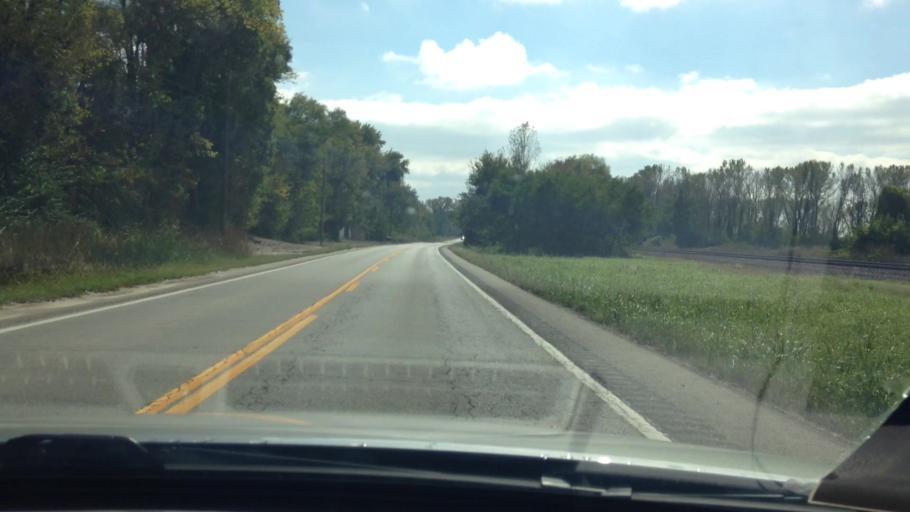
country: US
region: Kansas
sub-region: Leavenworth County
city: Leavenworth
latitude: 39.3122
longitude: -94.8511
